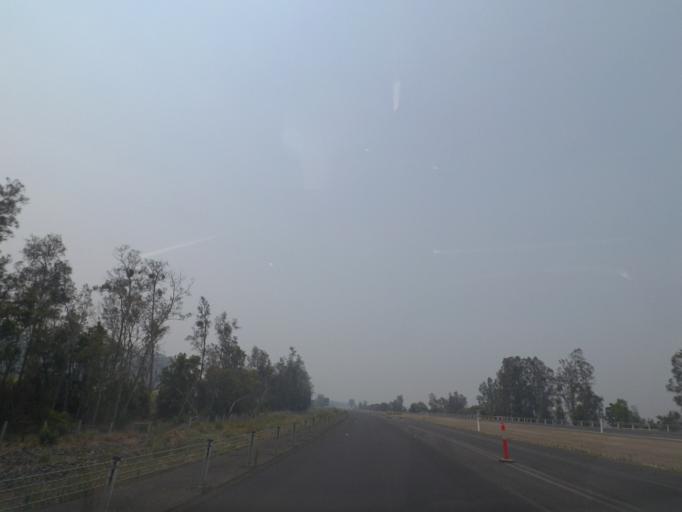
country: AU
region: New South Wales
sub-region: Ballina
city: Ballina
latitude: -28.8786
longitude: 153.4873
